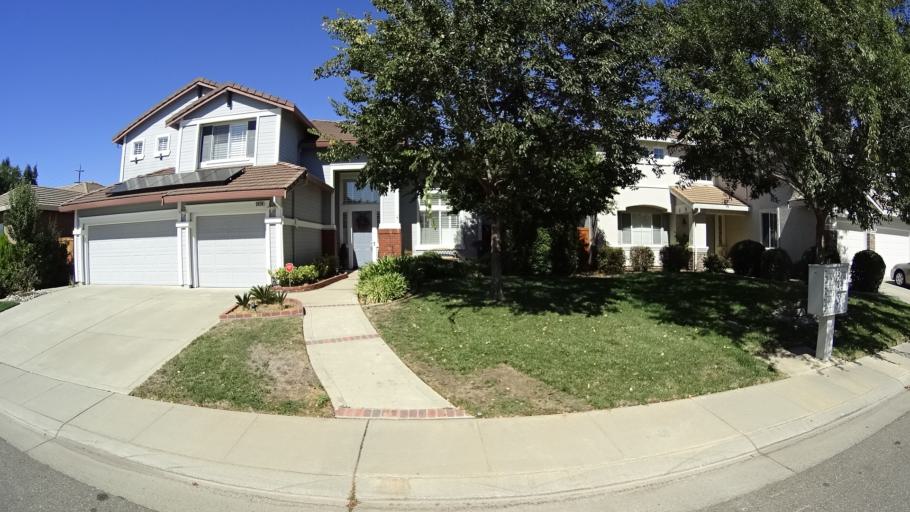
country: US
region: California
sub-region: Sacramento County
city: Laguna
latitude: 38.4157
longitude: -121.4645
